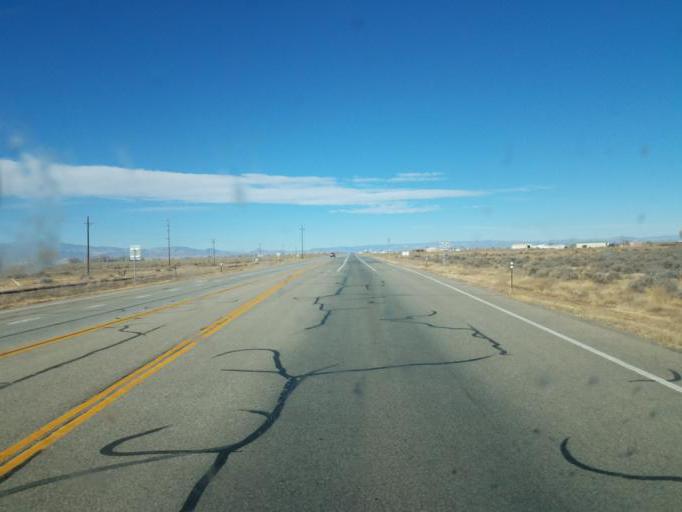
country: US
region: Colorado
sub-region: Alamosa County
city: Alamosa
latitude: 37.5123
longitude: -105.9820
